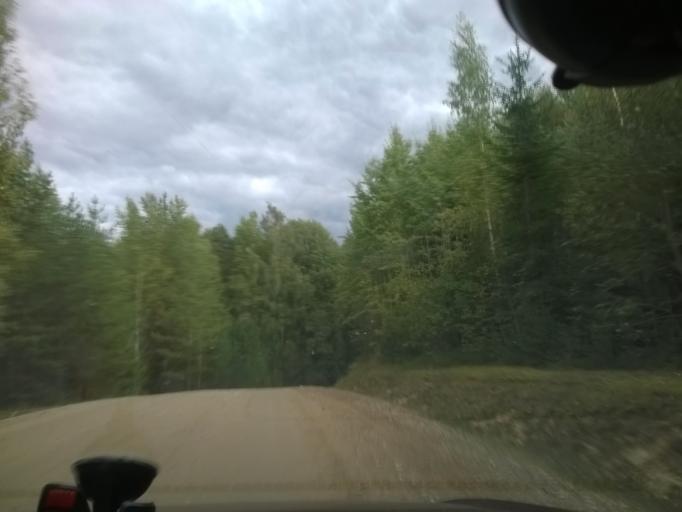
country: EE
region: Vorumaa
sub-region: Voru linn
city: Voru
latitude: 57.8178
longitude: 27.1429
